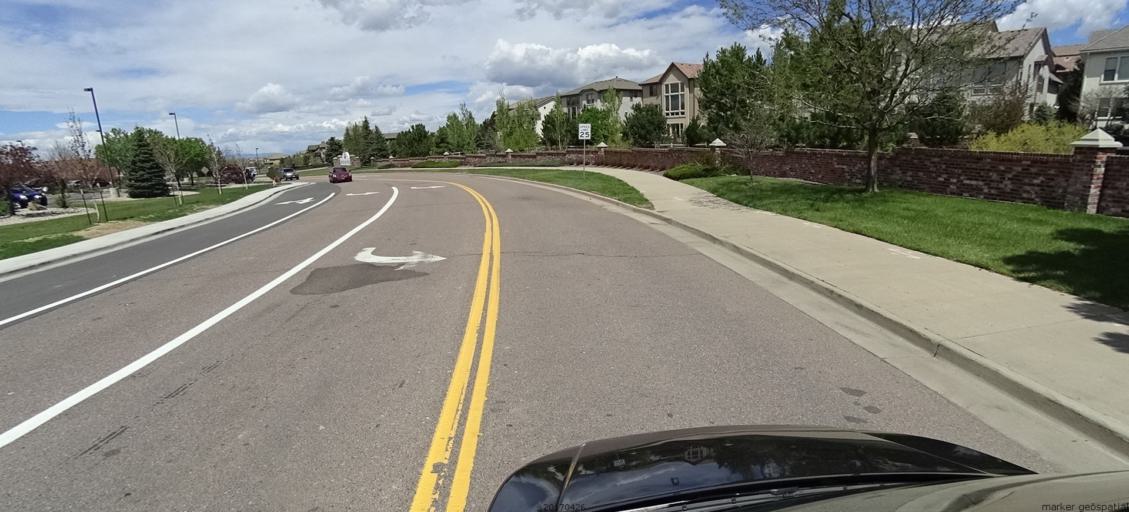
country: US
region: Colorado
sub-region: Adams County
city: Lone Tree
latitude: 39.5367
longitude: -104.8770
